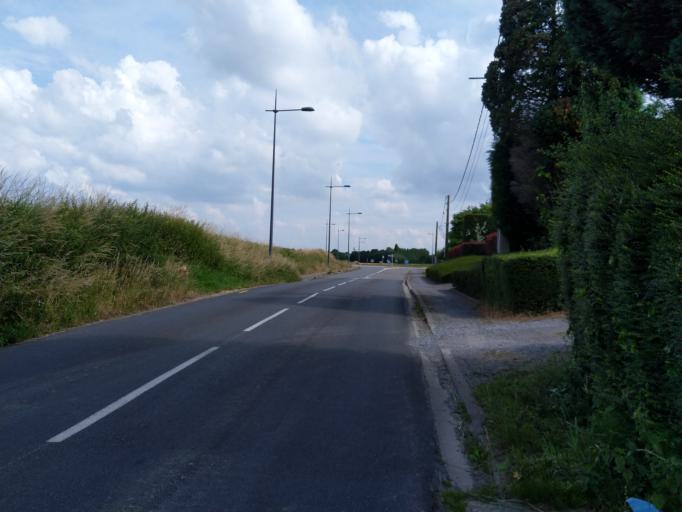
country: FR
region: Nord-Pas-de-Calais
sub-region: Departement du Nord
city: Rousies
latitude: 50.3106
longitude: 3.9994
